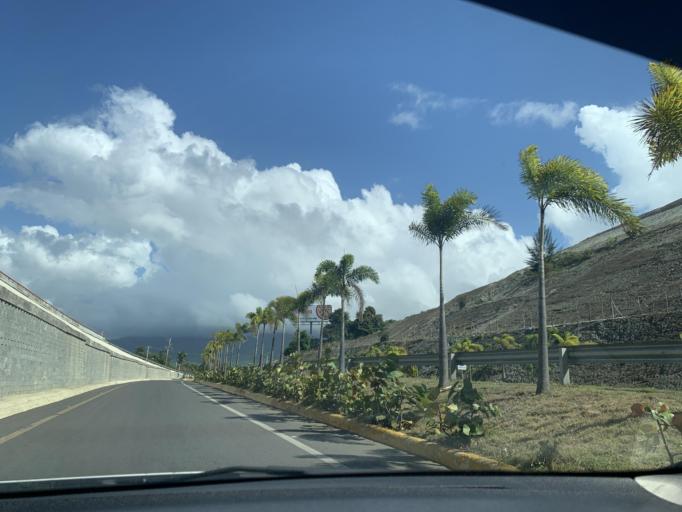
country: DO
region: Puerto Plata
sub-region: Puerto Plata
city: Puerto Plata
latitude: 19.8171
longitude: -70.7331
